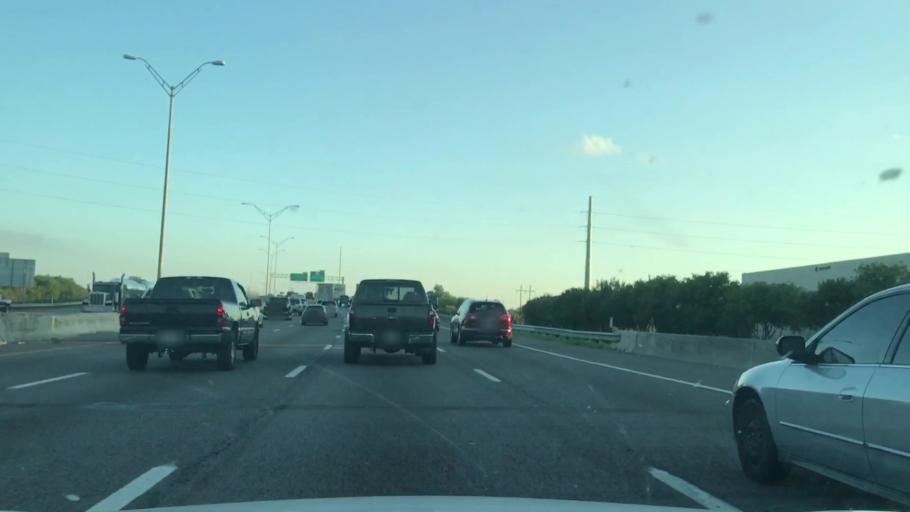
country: US
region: Texas
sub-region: Dallas County
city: Mesquite
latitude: 32.7754
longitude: -96.6243
